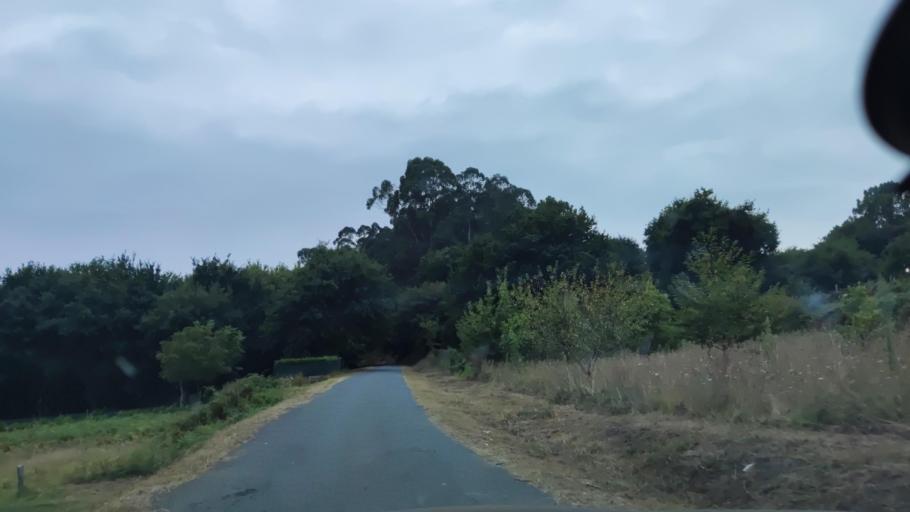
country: ES
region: Galicia
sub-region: Provincia de Pontevedra
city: Catoira
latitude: 42.7011
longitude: -8.7263
